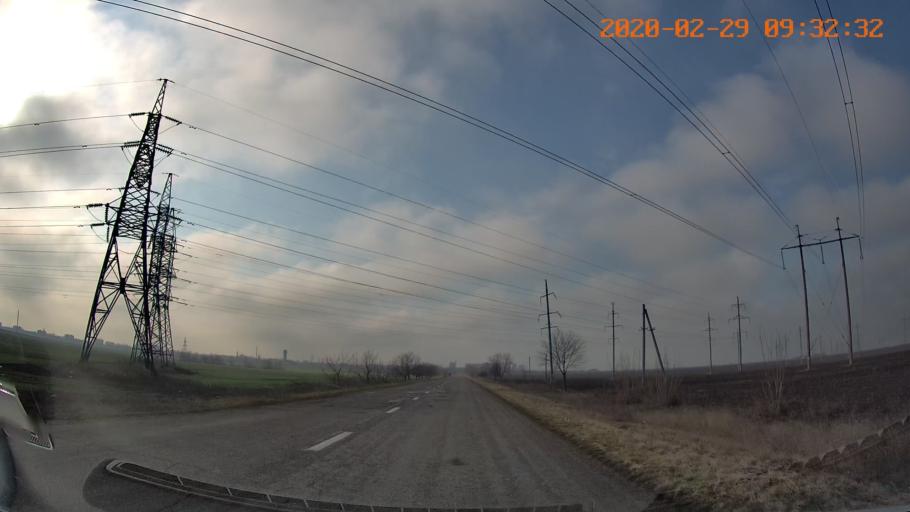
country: MD
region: Telenesti
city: Dnestrovsc
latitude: 46.6382
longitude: 29.9055
